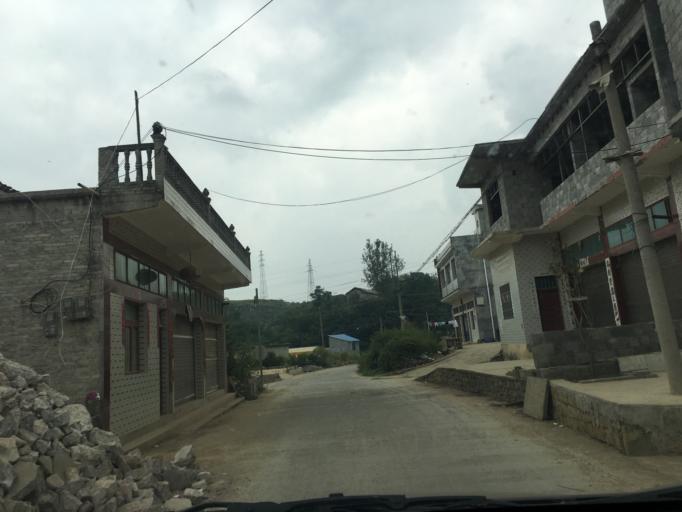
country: CN
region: Guangxi Zhuangzu Zizhiqu
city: Xinzhou
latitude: 25.5277
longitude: 105.6346
